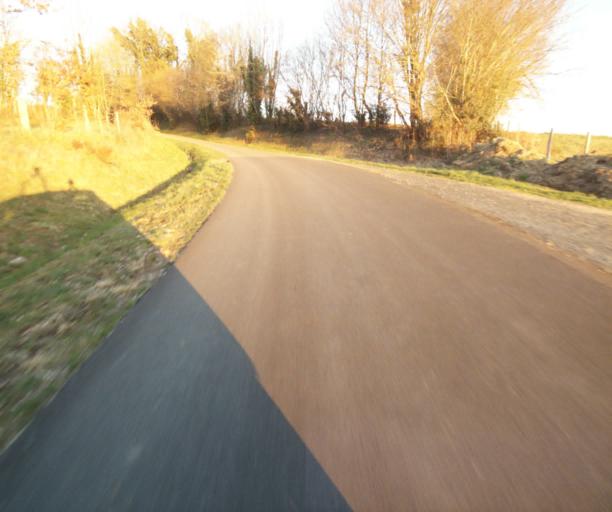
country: FR
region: Limousin
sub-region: Departement de la Correze
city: Saint-Mexant
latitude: 45.2948
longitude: 1.5982
